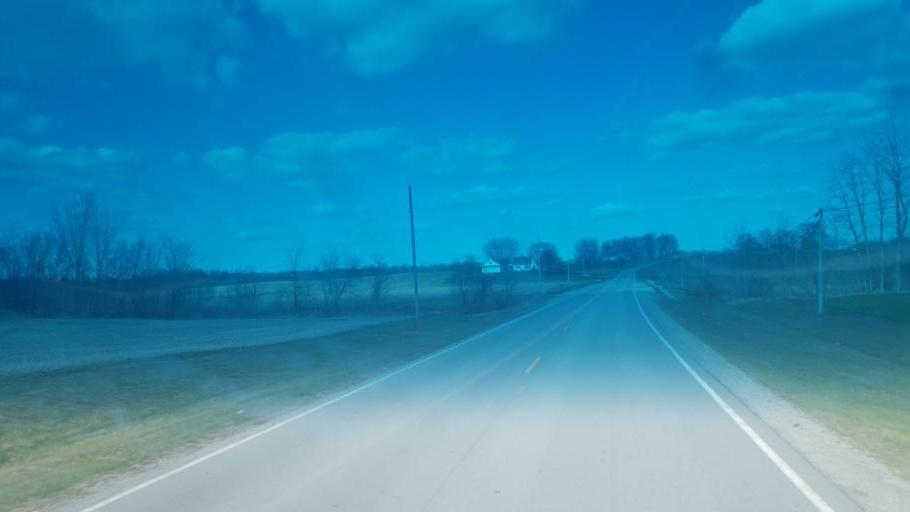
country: US
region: Ohio
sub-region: Highland County
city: Greenfield
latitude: 39.3365
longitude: -83.4049
